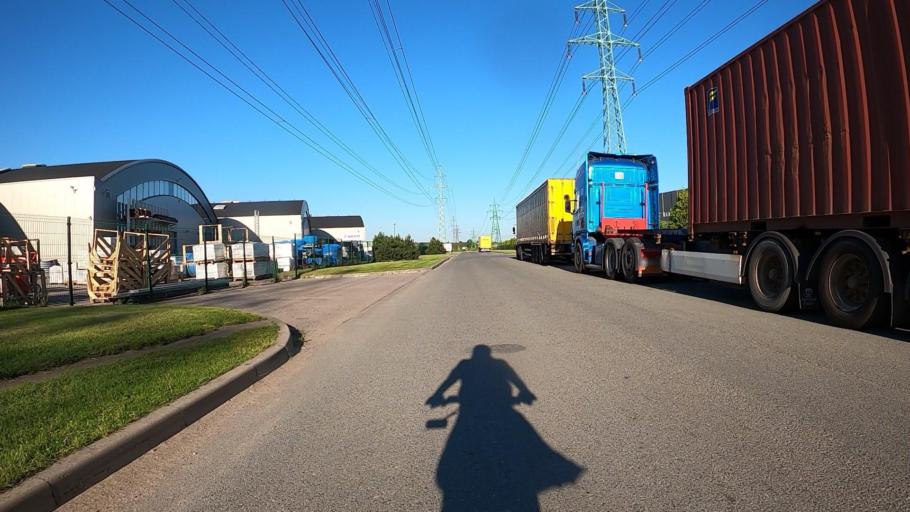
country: LV
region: Stopini
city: Ulbroka
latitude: 56.9299
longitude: 24.2367
